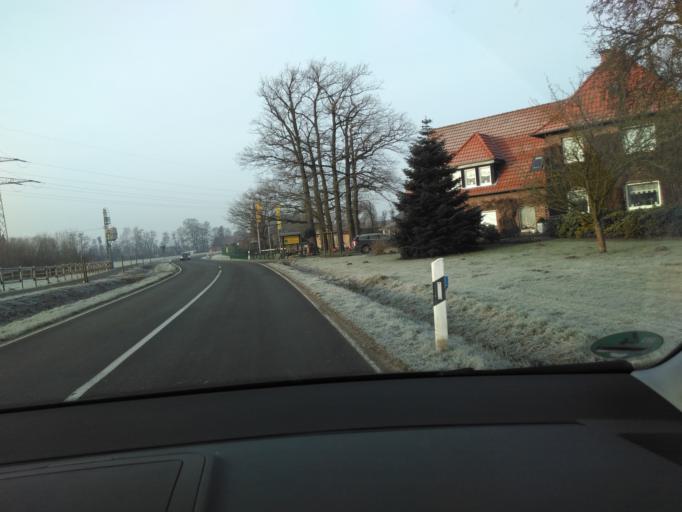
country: DE
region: North Rhine-Westphalia
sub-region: Regierungsbezirk Detmold
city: Verl
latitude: 51.8642
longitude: 8.4970
